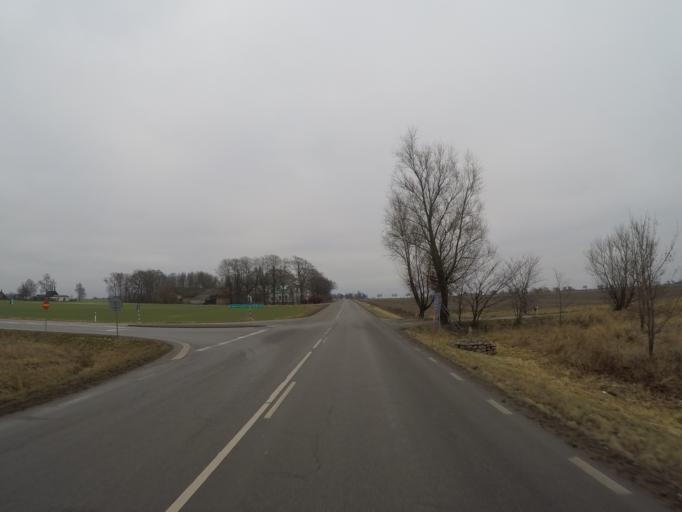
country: SE
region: Skane
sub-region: Hoors Kommun
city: Loberod
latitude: 55.7839
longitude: 13.4177
